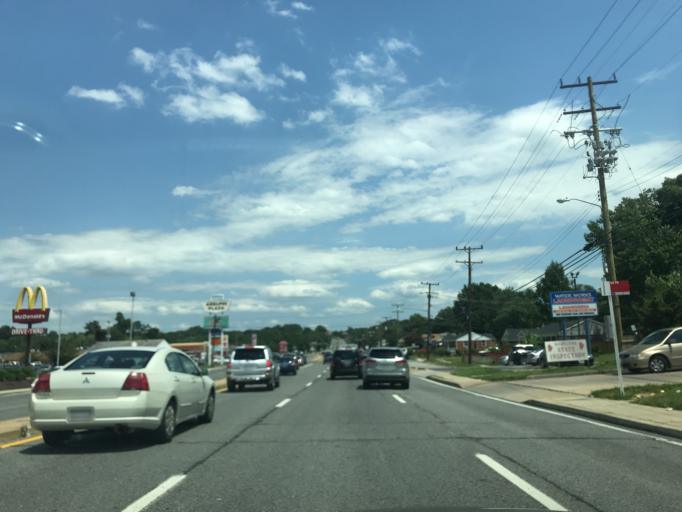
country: US
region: Maryland
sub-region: Prince George's County
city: Langley Park
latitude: 38.9841
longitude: -76.9712
